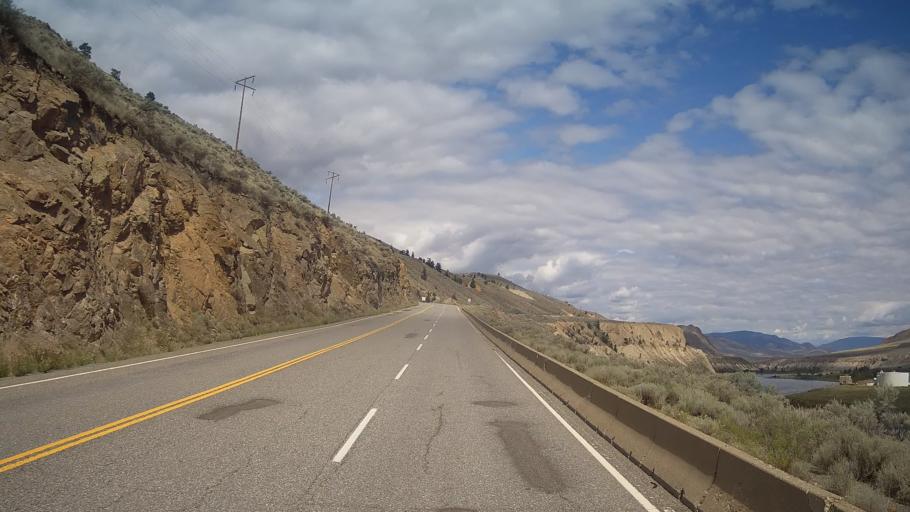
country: CA
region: British Columbia
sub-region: Thompson-Nicola Regional District
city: Ashcroft
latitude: 50.5506
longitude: -121.2955
